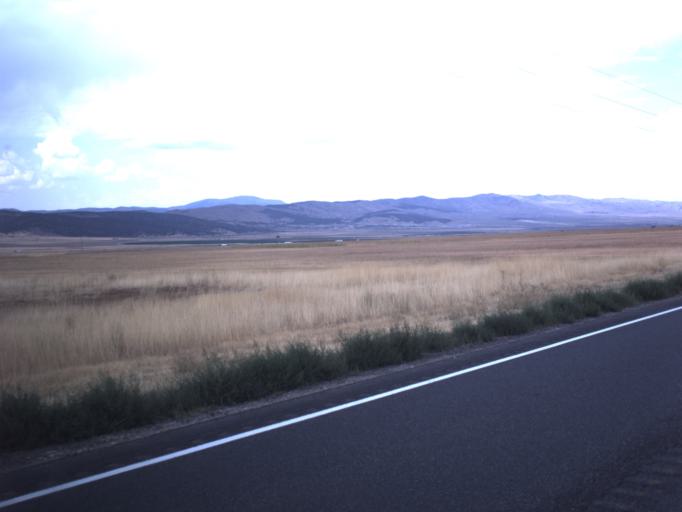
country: US
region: Utah
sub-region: Juab County
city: Nephi
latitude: 39.6424
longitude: -111.8614
